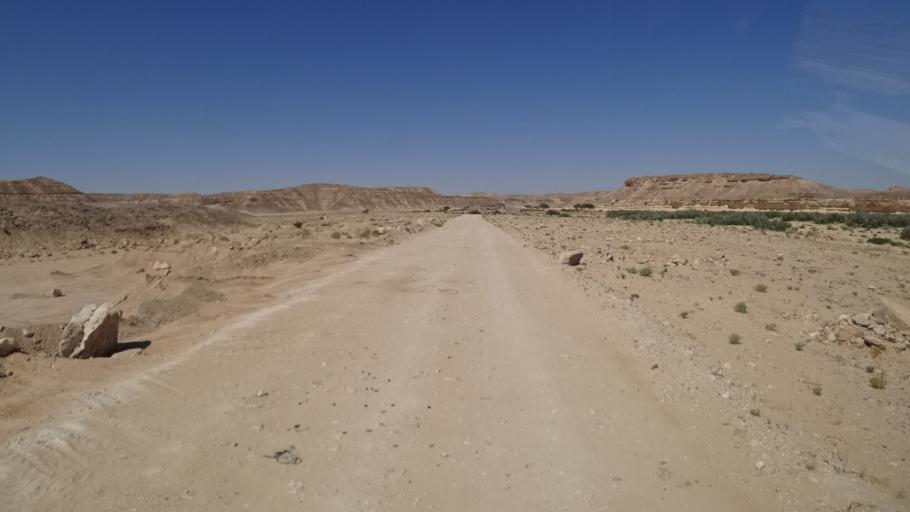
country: OM
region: Zufar
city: Salalah
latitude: 17.5006
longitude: 53.3653
